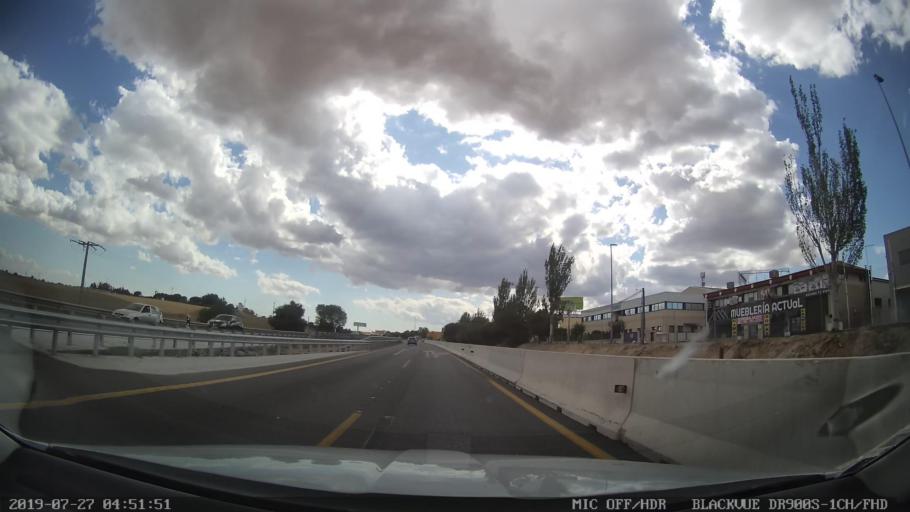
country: ES
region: Madrid
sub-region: Provincia de Madrid
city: Navalcarnero
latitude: 40.2897
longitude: -3.9910
